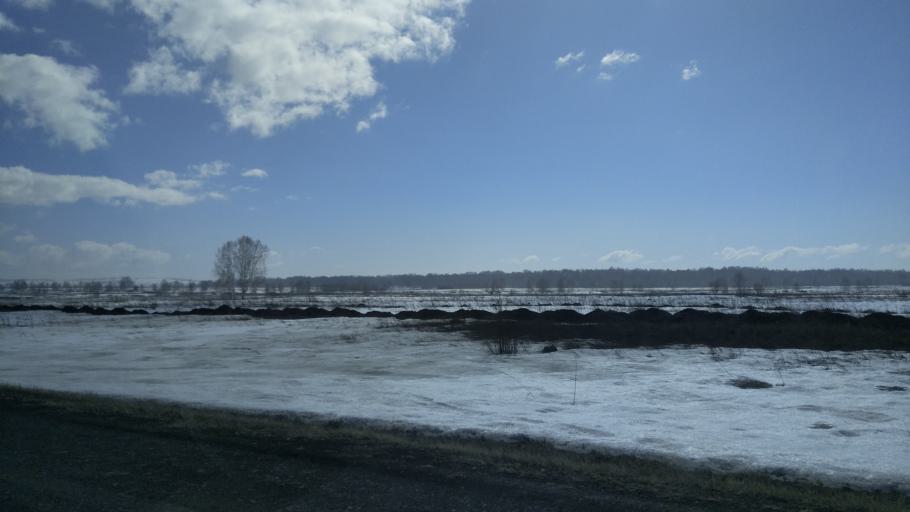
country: RU
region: Kemerovo
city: Yurga
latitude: 55.6835
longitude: 85.0128
